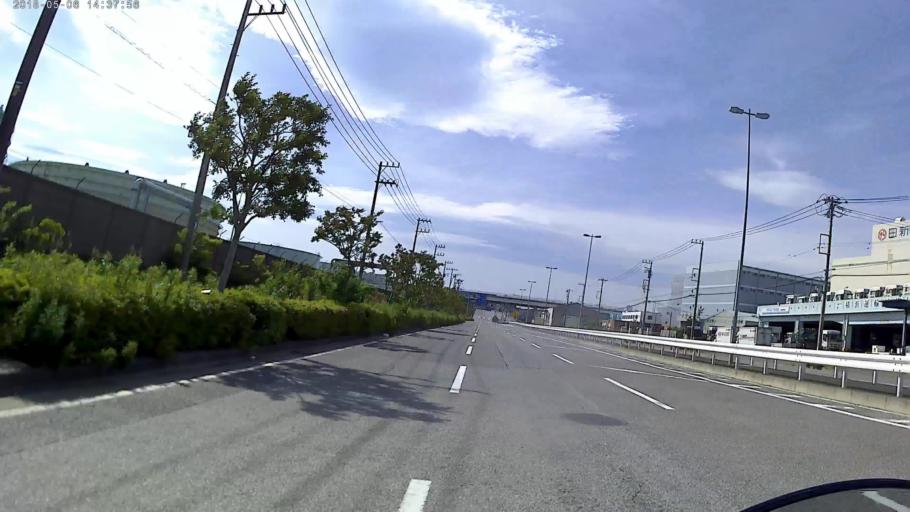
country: JP
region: Kanagawa
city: Yokohama
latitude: 35.4128
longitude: 139.6726
